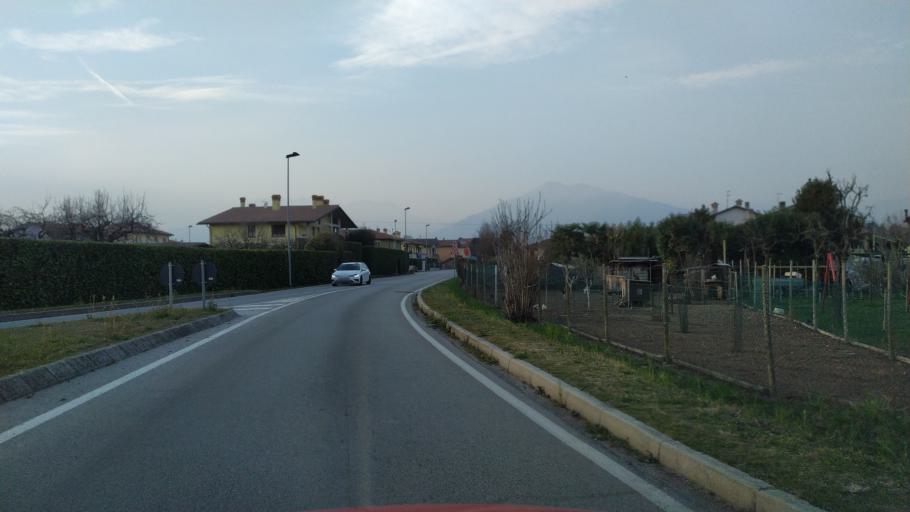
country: IT
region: Veneto
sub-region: Provincia di Vicenza
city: Marano Vicentino
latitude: 45.6897
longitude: 11.4447
